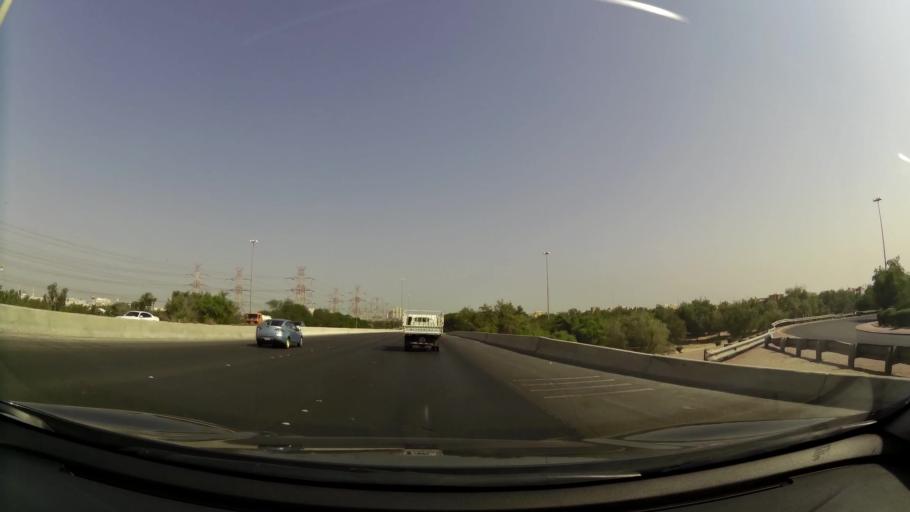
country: KW
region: Mubarak al Kabir
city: Sabah as Salim
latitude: 29.2646
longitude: 48.0443
